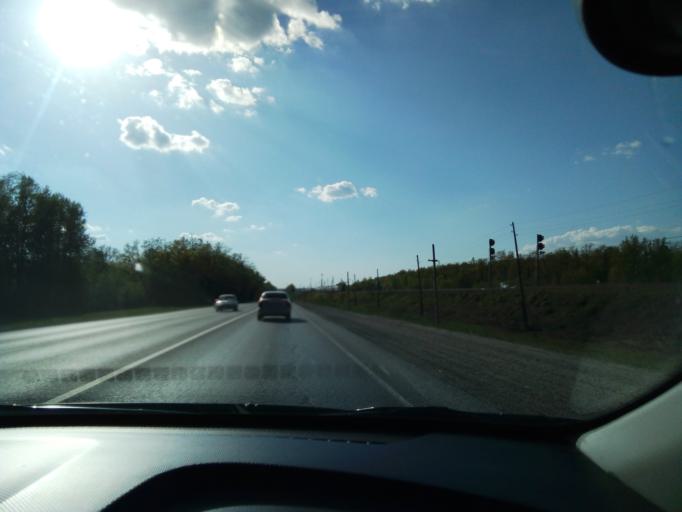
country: RU
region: Chuvashia
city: Novyye Lapsary
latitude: 56.0738
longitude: 47.2078
